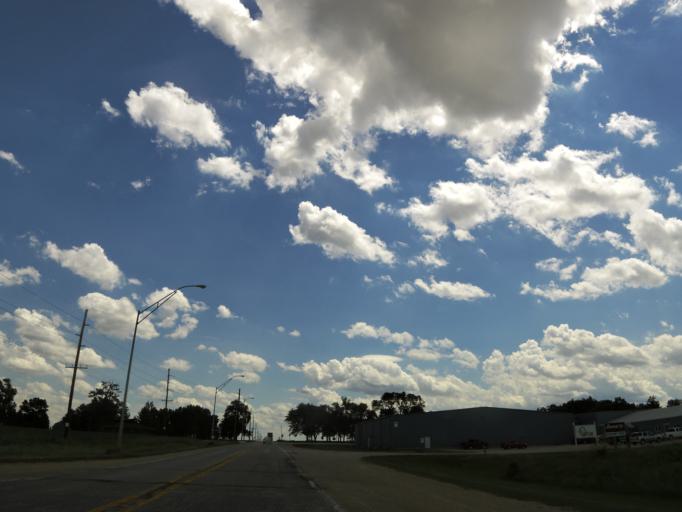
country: US
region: Iowa
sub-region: Buchanan County
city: Independence
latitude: 42.4452
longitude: -91.8902
